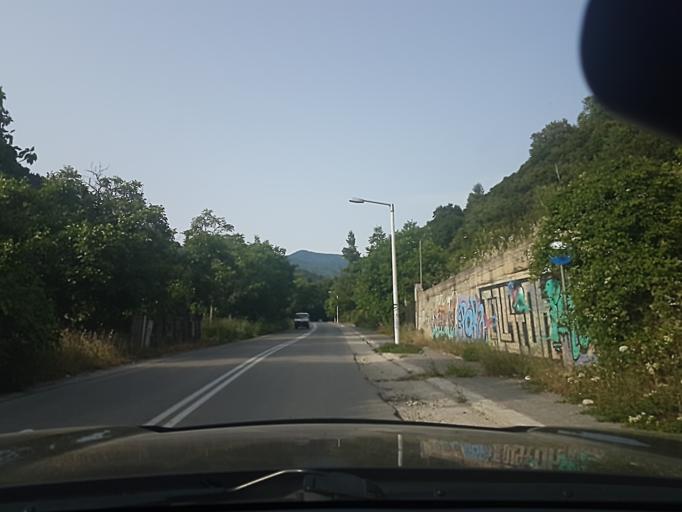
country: GR
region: Central Greece
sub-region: Nomos Evvoias
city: Yimnon
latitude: 38.5767
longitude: 23.8324
